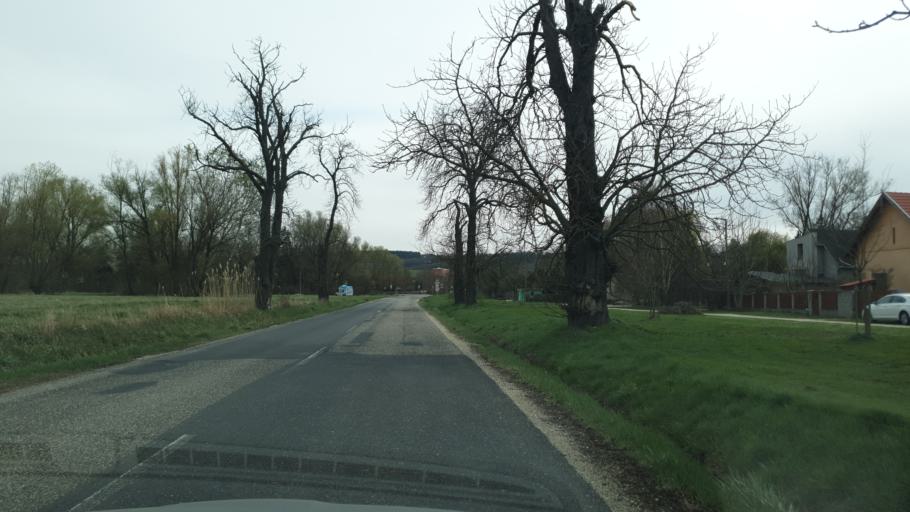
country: HU
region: Fejer
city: Etyek
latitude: 47.4588
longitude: 18.7261
